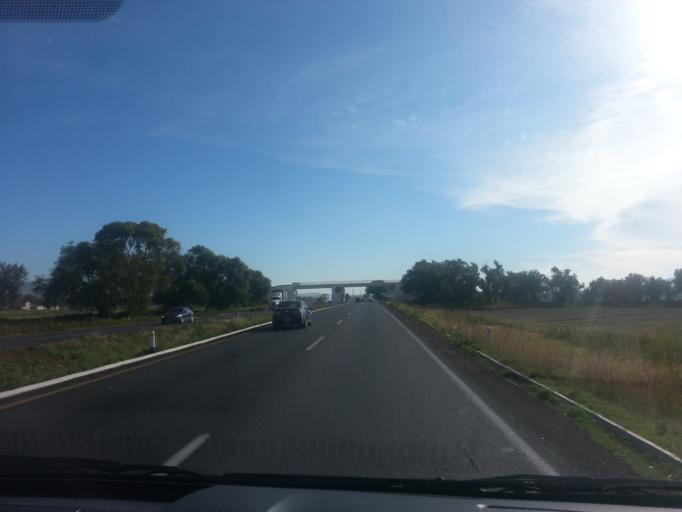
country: MX
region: Mexico
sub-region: Acolman de Nezahualcoyotl
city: San Pedro Tepetitlan
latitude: 19.6363
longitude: -98.9036
